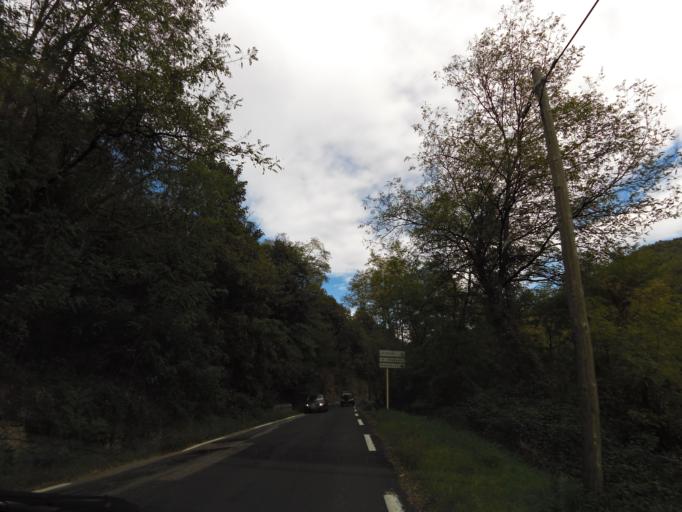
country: FR
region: Languedoc-Roussillon
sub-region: Departement du Gard
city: Lasalle
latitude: 44.0198
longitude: 3.8561
